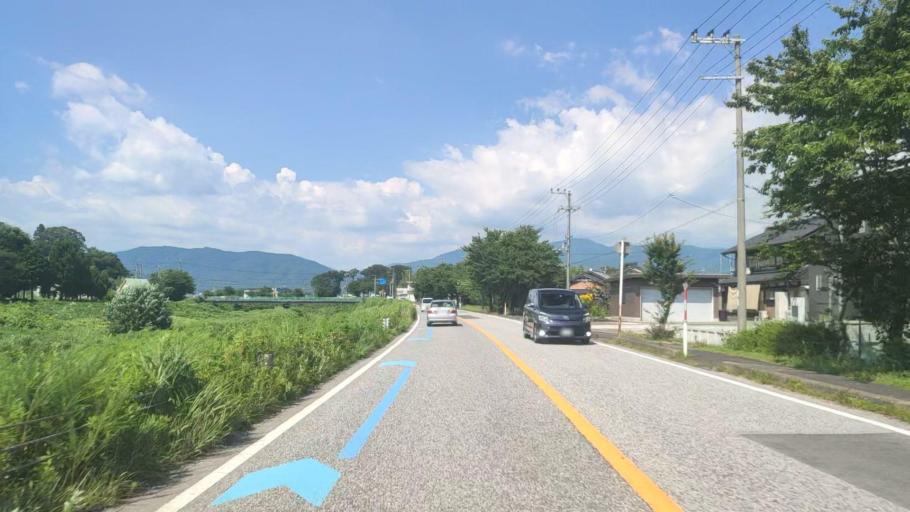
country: JP
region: Shiga Prefecture
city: Nagahama
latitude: 35.4700
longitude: 136.2115
